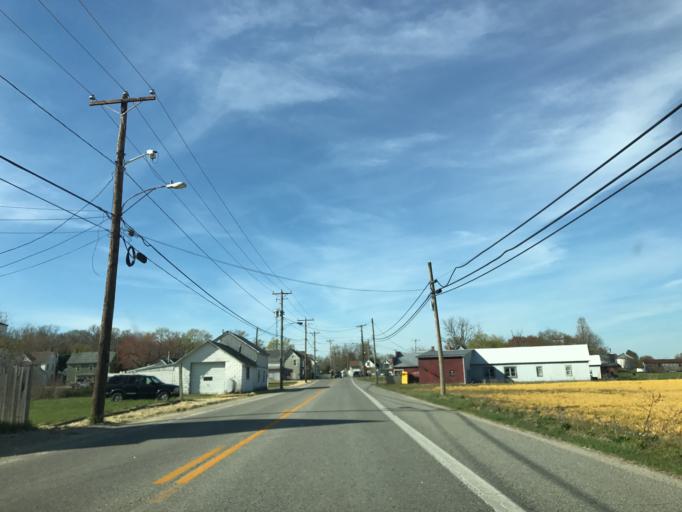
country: US
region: Maryland
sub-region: Caroline County
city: Greensboro
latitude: 39.0319
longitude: -75.7870
